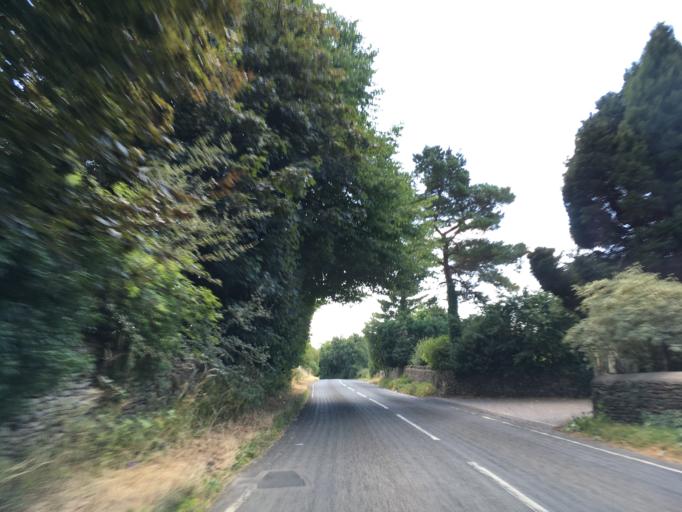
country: GB
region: England
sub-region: Gloucestershire
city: Stroud
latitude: 51.7715
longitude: -2.2355
